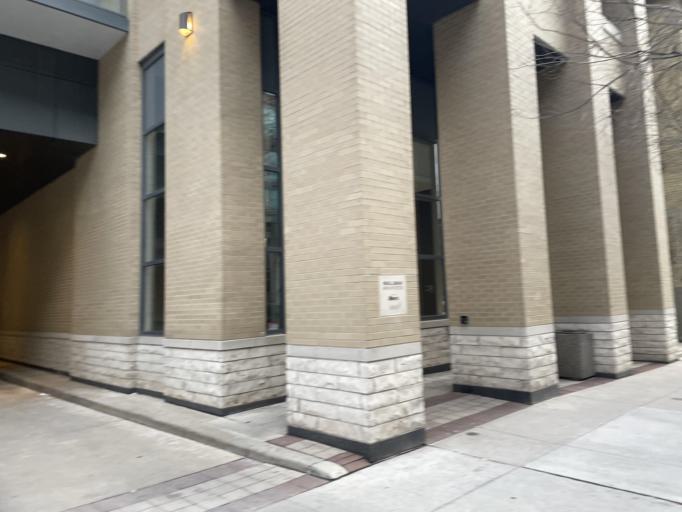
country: CA
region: Ontario
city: Toronto
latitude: 43.6522
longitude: -79.3712
